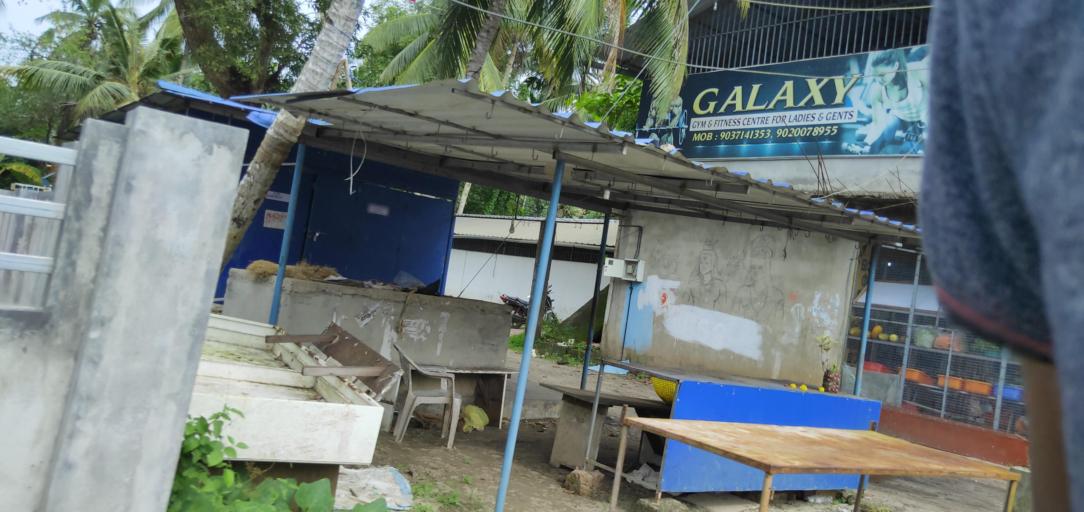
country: IN
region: Kerala
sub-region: Alappuzha
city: Kayankulam
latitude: 9.2158
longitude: 76.4616
